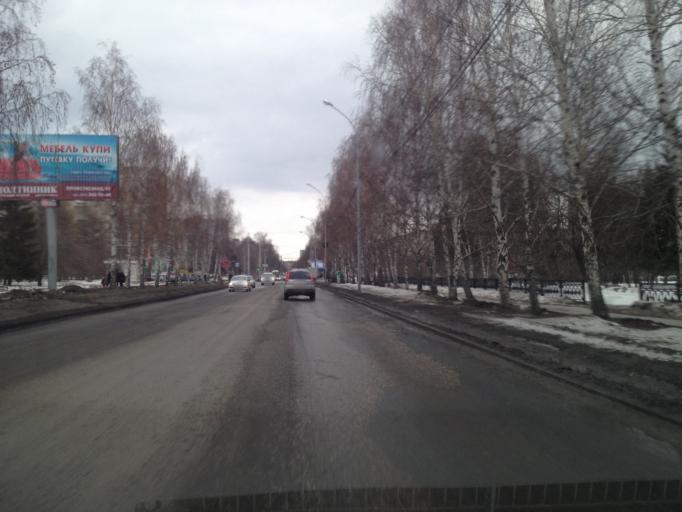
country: RU
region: Sverdlovsk
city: Sovkhoznyy
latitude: 56.8030
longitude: 60.5652
